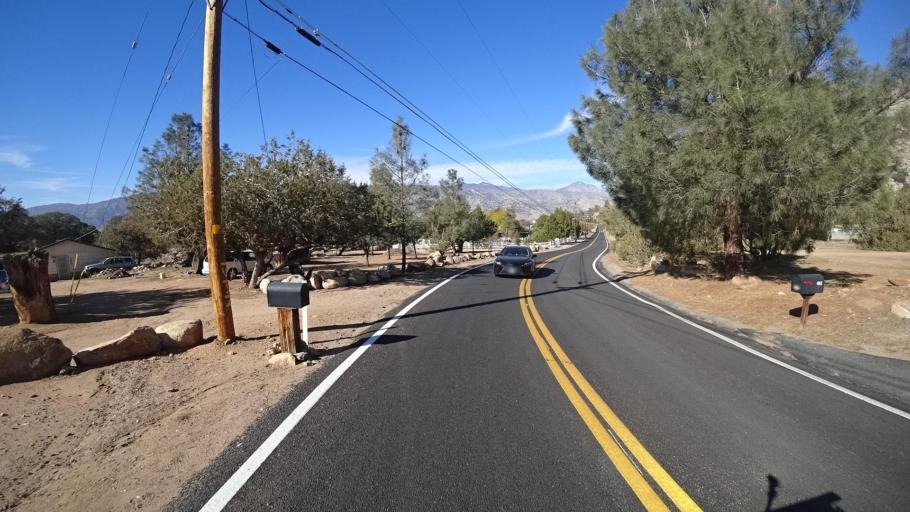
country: US
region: California
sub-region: Kern County
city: Lake Isabella
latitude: 35.6023
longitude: -118.4604
